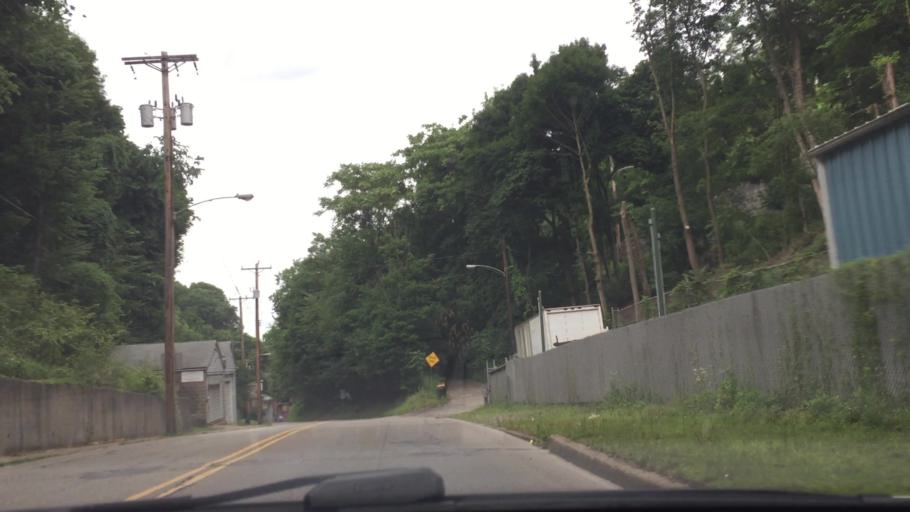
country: US
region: Pennsylvania
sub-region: Allegheny County
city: McKees Rocks
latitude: 40.4753
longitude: -80.0701
